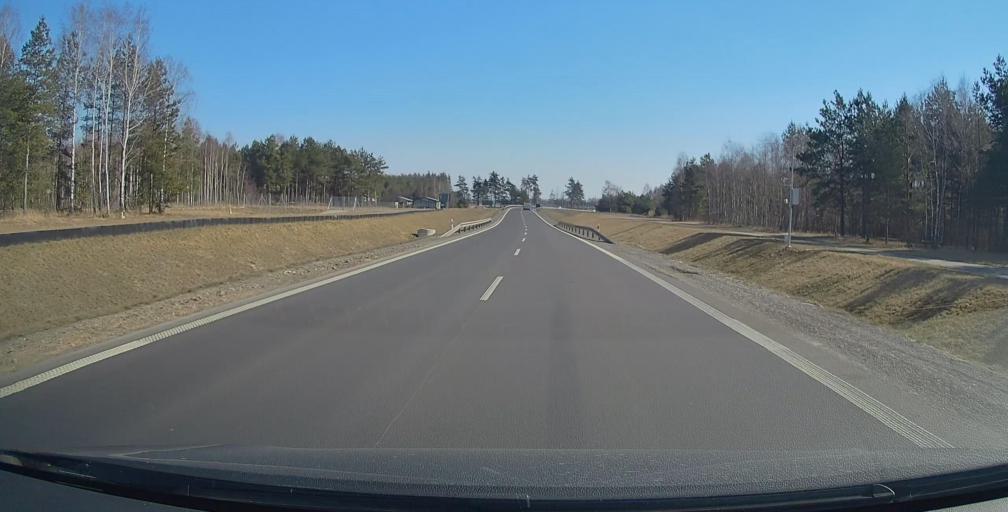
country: PL
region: Subcarpathian Voivodeship
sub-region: Powiat nizanski
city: Raclawice
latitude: 50.4957
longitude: 22.1886
